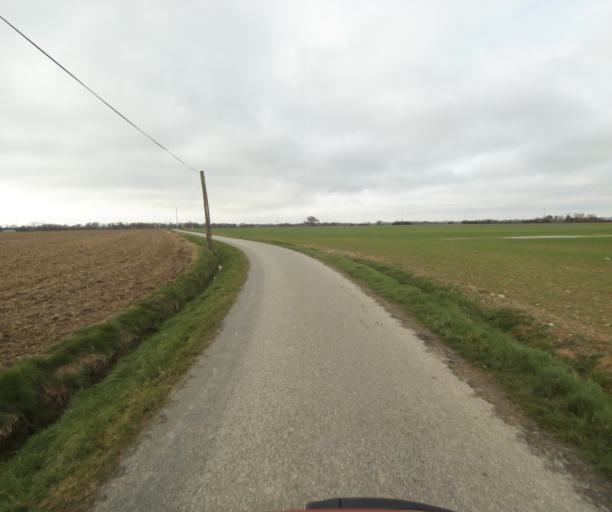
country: FR
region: Languedoc-Roussillon
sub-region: Departement de l'Aude
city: Belpech
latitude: 43.1802
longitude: 1.7151
